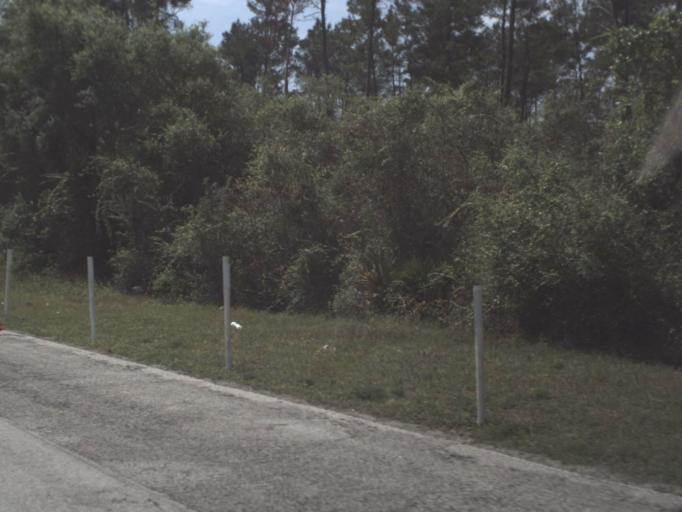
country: US
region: Florida
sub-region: Lake County
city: Astor
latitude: 29.1762
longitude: -81.6474
